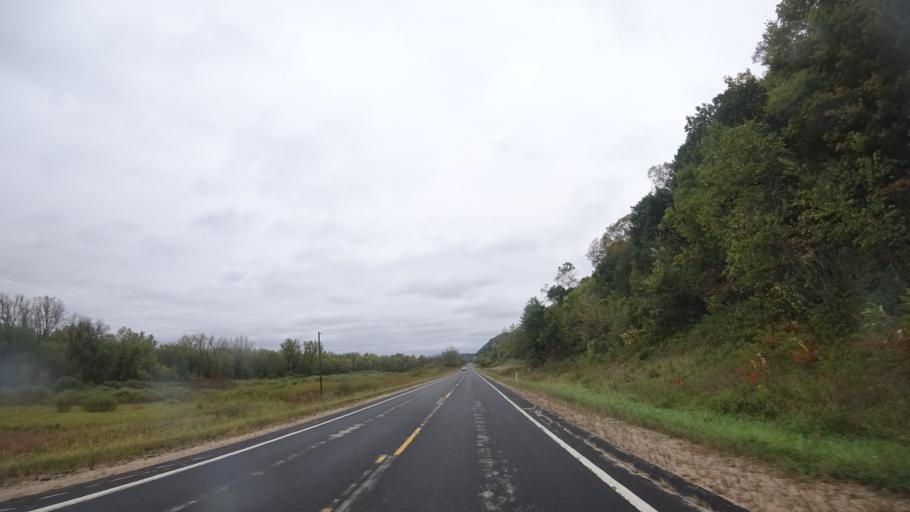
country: US
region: Wisconsin
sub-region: Grant County
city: Boscobel
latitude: 43.1925
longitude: -90.6611
